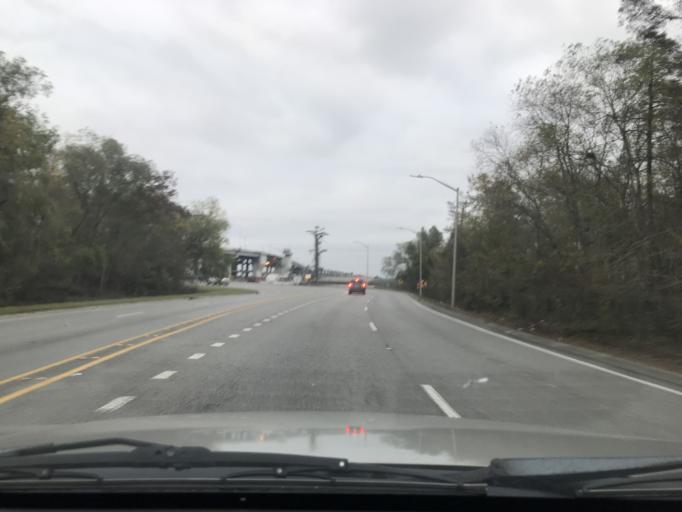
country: US
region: Louisiana
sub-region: Jefferson Parish
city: Woodmere
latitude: 29.8695
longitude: -90.0730
